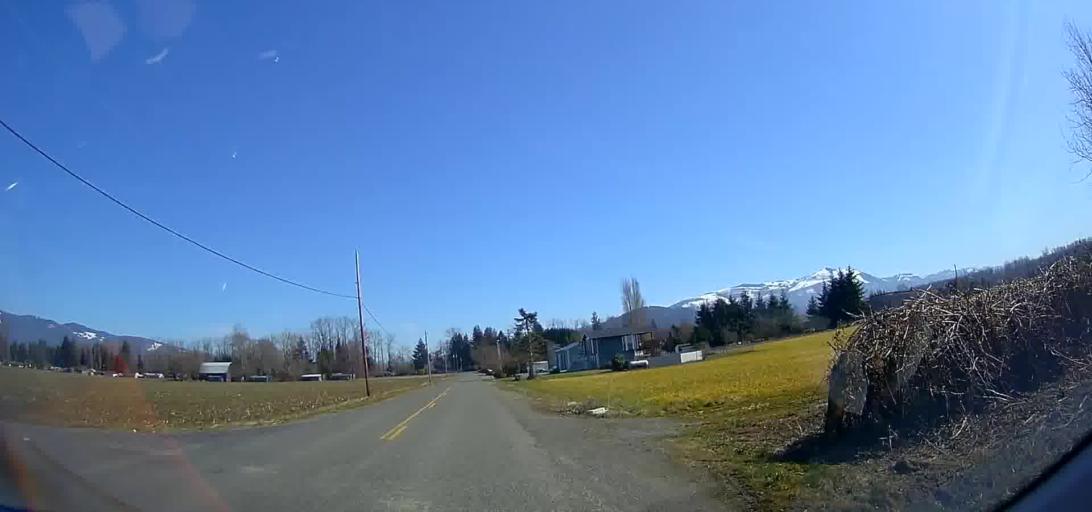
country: US
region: Washington
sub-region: Skagit County
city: Sedro-Woolley
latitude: 48.4893
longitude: -122.2802
